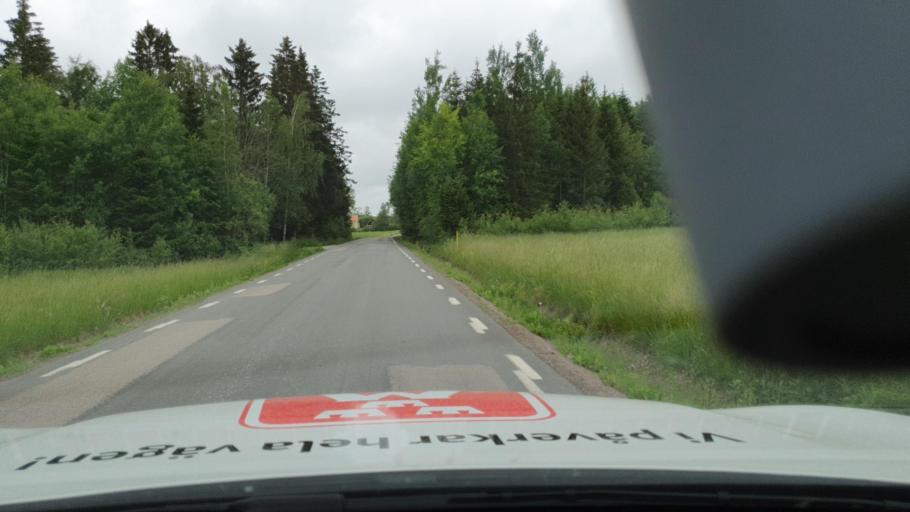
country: SE
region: Vaestra Goetaland
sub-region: Tibro Kommun
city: Tibro
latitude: 58.3790
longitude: 14.0523
